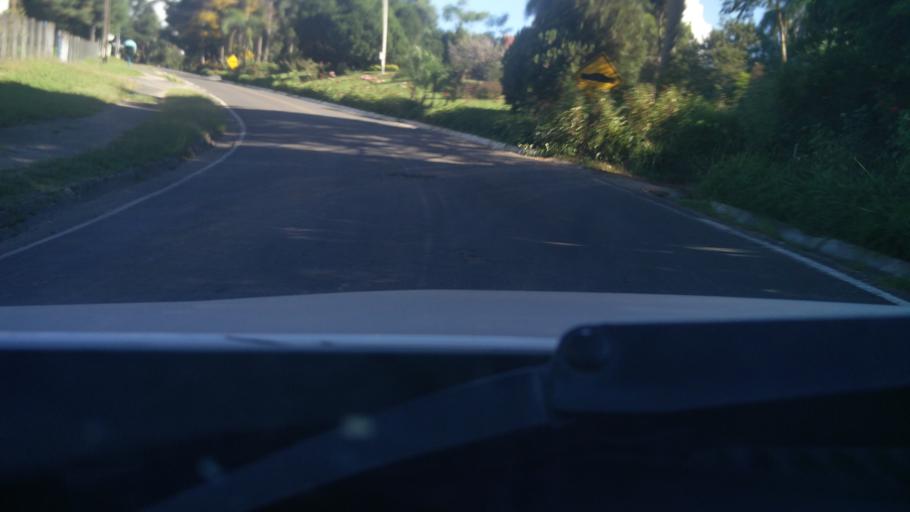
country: BR
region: Parana
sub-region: Palmeira
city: Palmeira
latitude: -25.4277
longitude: -49.8229
